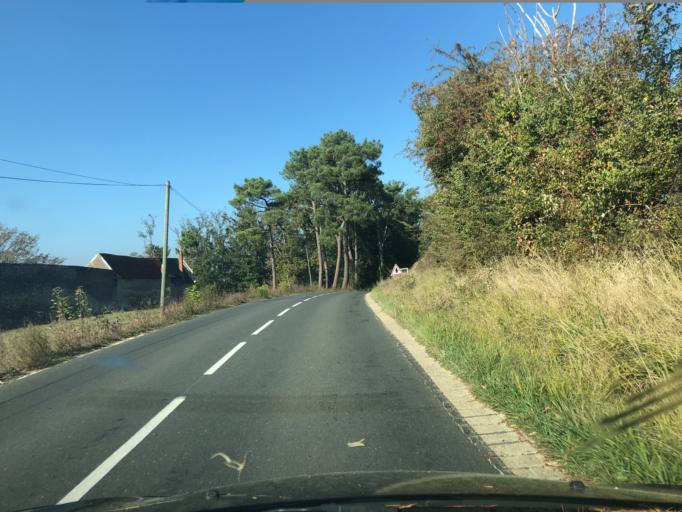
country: FR
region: Centre
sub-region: Departement d'Indre-et-Loire
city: Mettray
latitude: 47.4738
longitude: 0.6641
